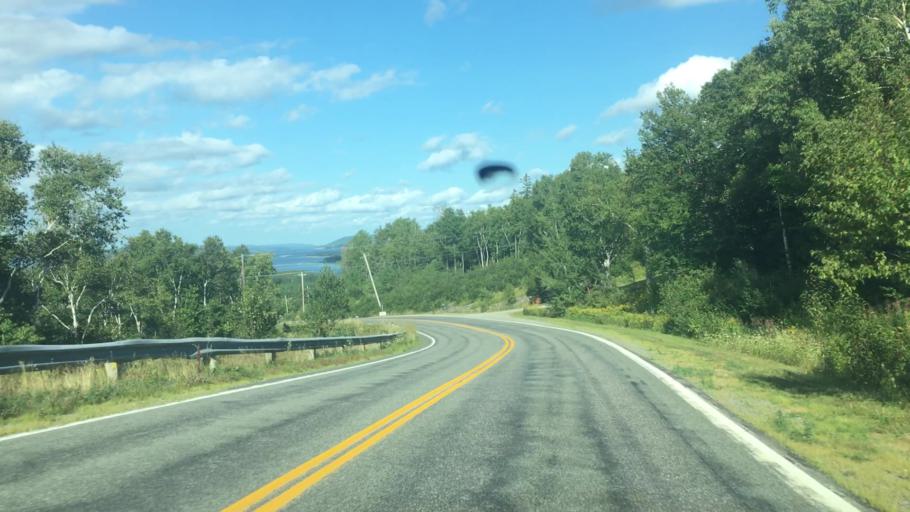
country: CA
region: Nova Scotia
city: Sydney
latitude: 45.8643
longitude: -60.6238
